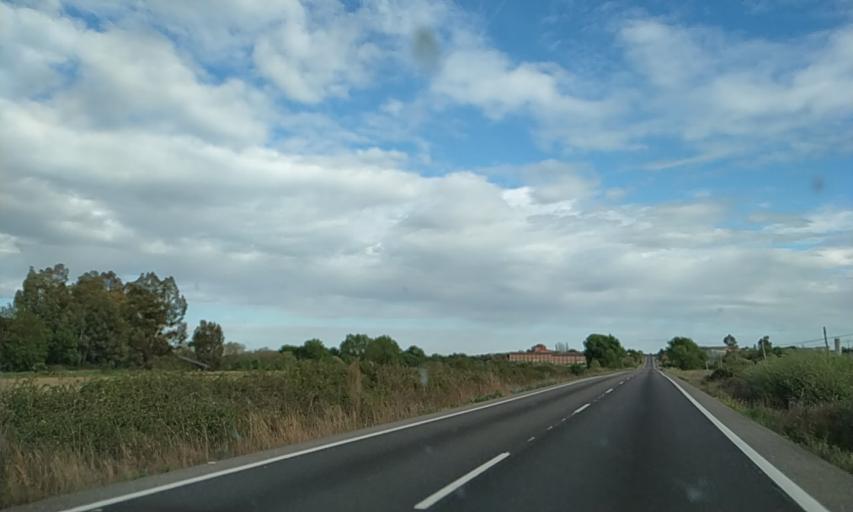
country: ES
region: Extremadura
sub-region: Provincia de Caceres
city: Huelaga
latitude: 40.0421
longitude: -6.6321
